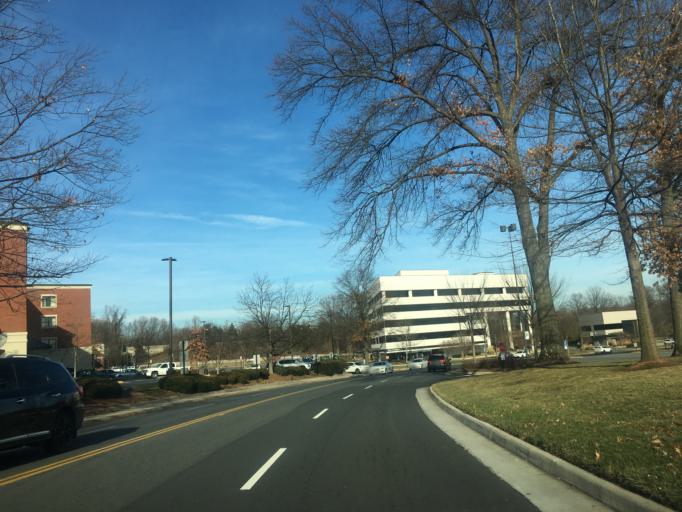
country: US
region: Virginia
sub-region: Fairfax County
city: Greenbriar
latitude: 38.8649
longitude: -77.3623
